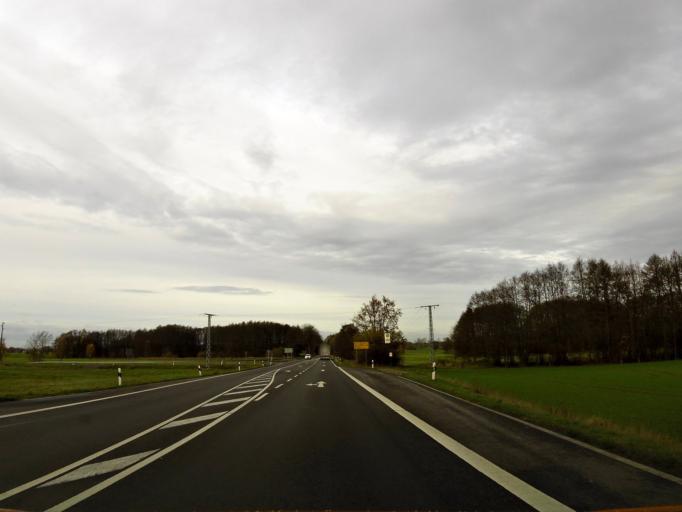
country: DE
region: Saxony-Anhalt
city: Klotze
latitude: 52.6866
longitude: 11.2663
